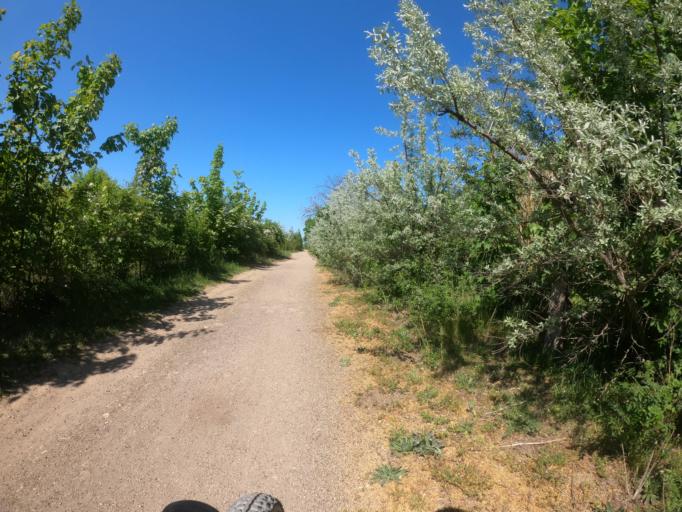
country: DE
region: Hesse
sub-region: Regierungsbezirk Darmstadt
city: Florsheim
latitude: 50.0094
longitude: 8.3971
